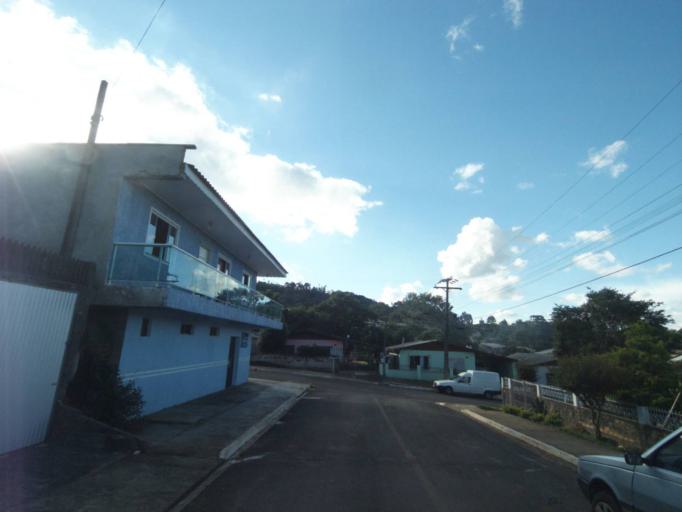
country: BR
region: Parana
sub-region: Uniao Da Vitoria
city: Uniao da Vitoria
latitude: -26.1673
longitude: -51.5353
